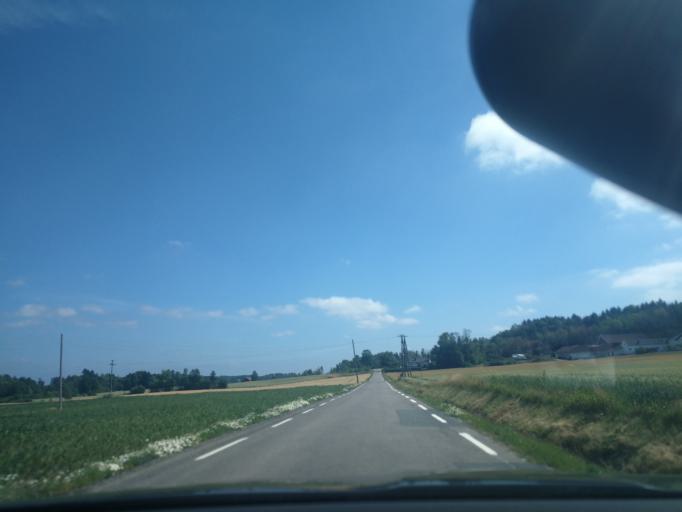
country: NO
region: Vestfold
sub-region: Stokke
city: Stokke
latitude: 59.2076
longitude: 10.2695
